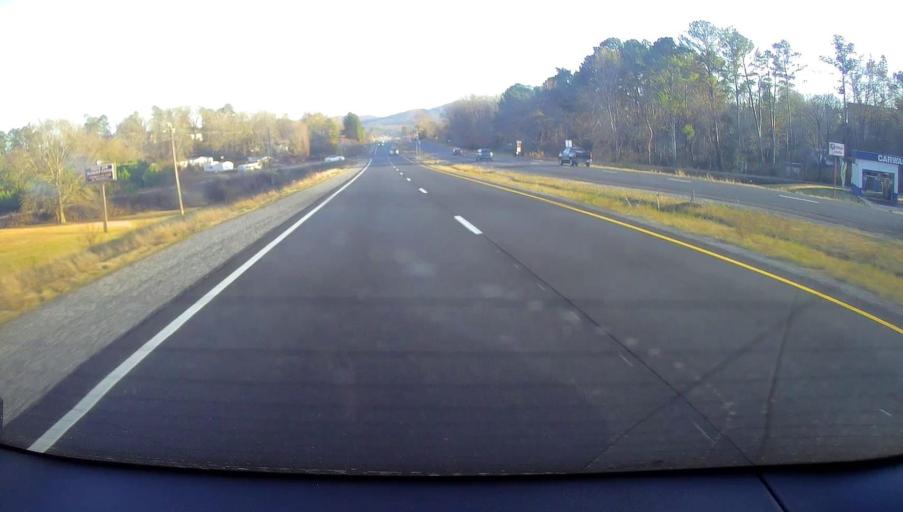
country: US
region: Alabama
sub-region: Calhoun County
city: Saks
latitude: 33.7108
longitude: -85.8398
